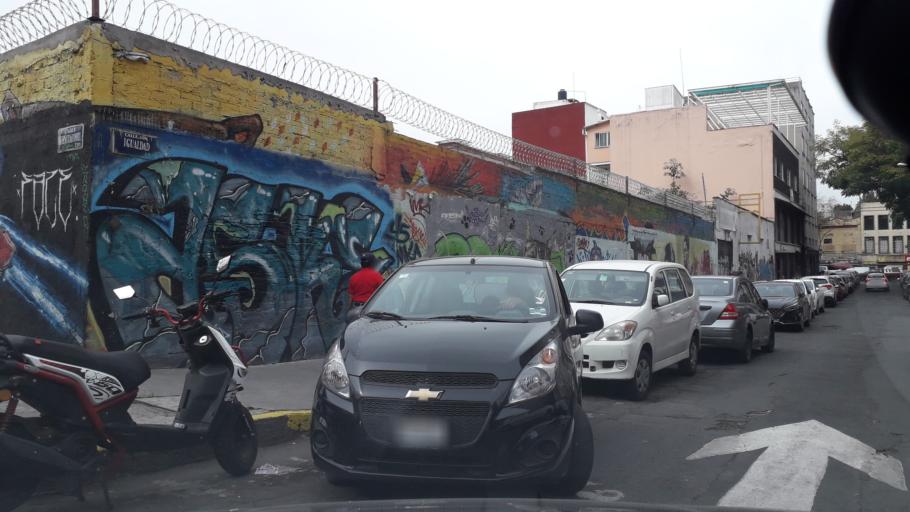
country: MX
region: Mexico City
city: Mexico City
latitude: 19.4257
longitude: -99.1403
